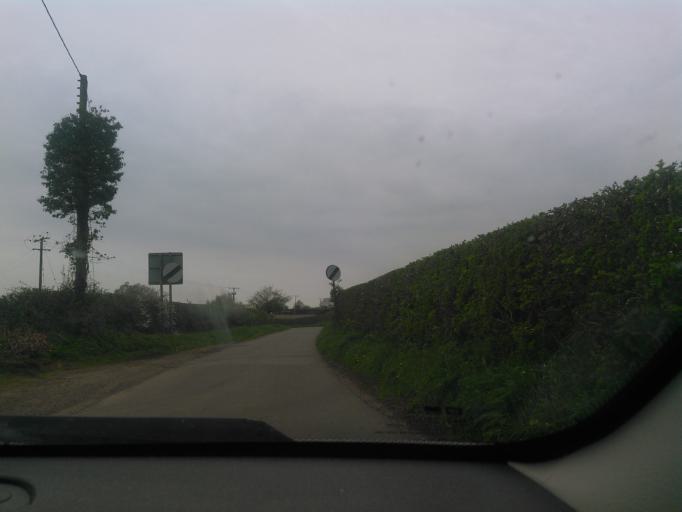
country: GB
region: England
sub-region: Shropshire
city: Stoke upon Tern
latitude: 52.7867
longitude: -2.5610
